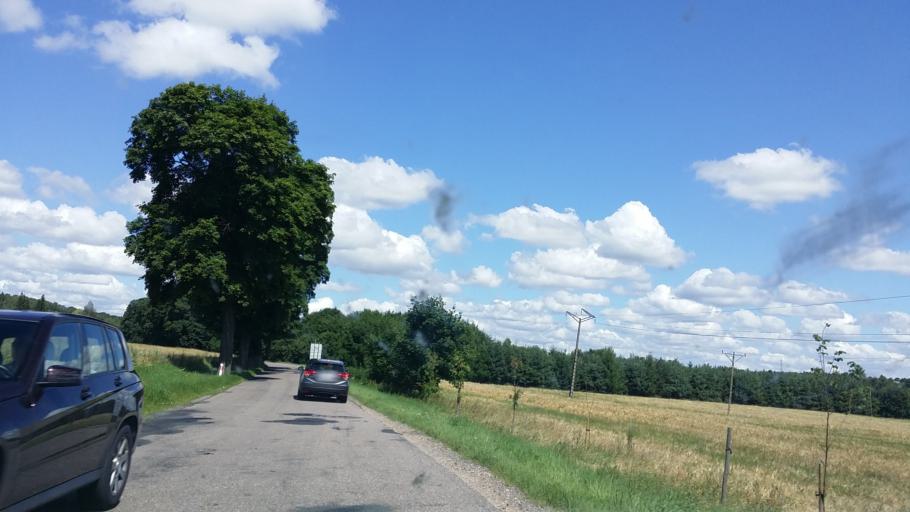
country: PL
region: West Pomeranian Voivodeship
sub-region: Powiat swidwinski
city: Swidwin
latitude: 53.7469
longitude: 15.7716
